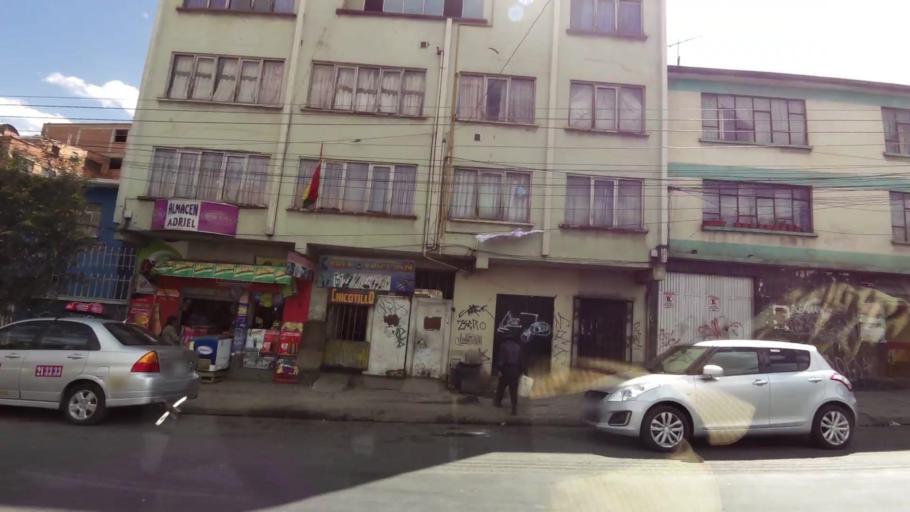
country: BO
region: La Paz
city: La Paz
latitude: -16.4865
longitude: -68.1244
